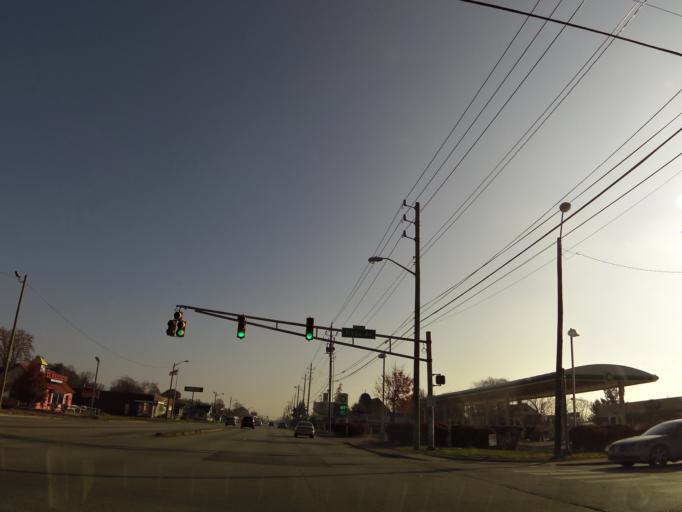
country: US
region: Indiana
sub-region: Marion County
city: Speedway
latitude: 39.7878
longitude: -86.2161
